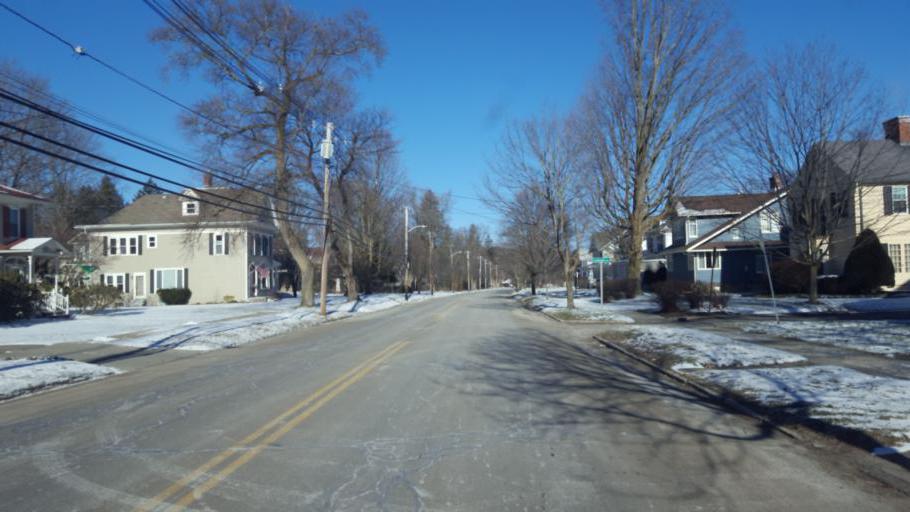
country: US
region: New York
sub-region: Allegany County
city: Wellsville
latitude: 42.1257
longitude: -77.9544
